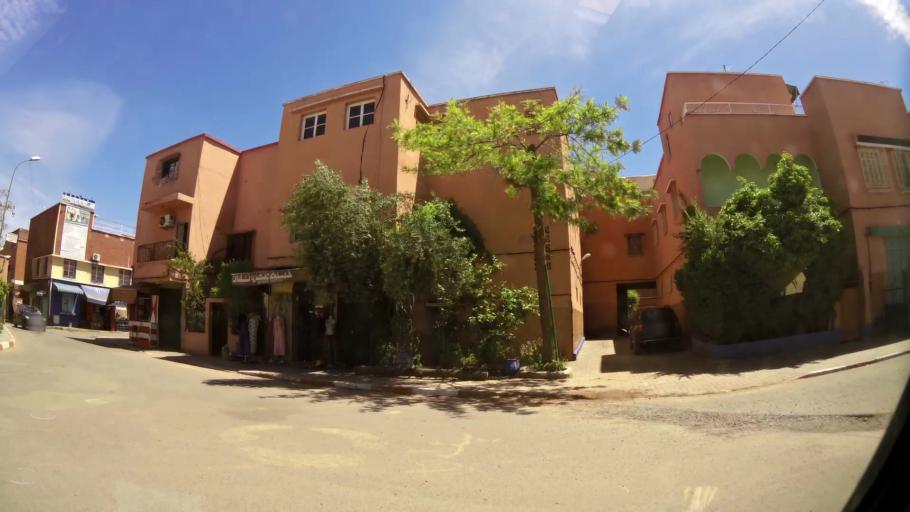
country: MA
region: Marrakech-Tensift-Al Haouz
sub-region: Marrakech
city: Marrakesh
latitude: 31.6561
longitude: -8.0022
